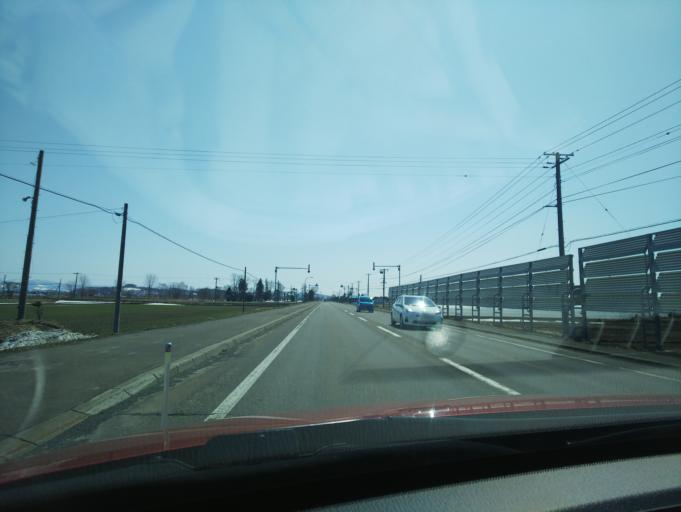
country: JP
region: Hokkaido
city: Nayoro
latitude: 44.2073
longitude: 142.3949
